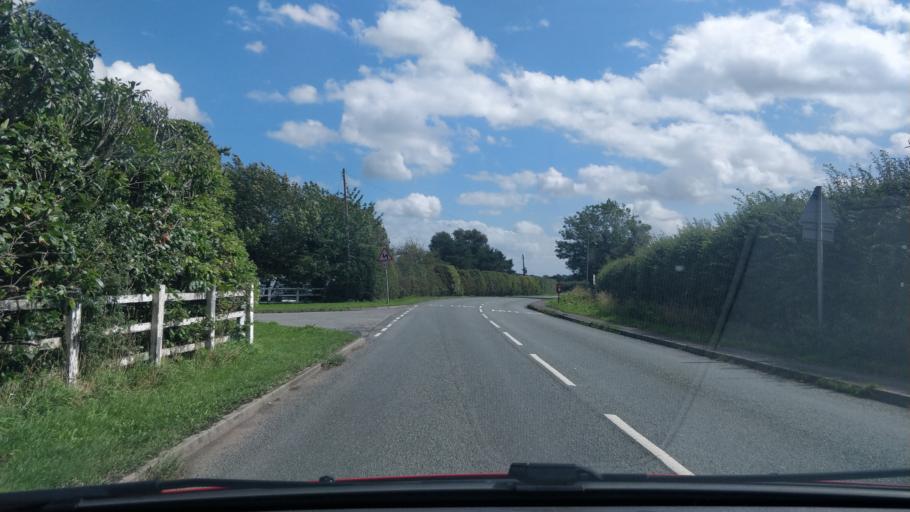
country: GB
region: England
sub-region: Cheshire West and Chester
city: Eccleston
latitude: 53.1545
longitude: -2.9237
